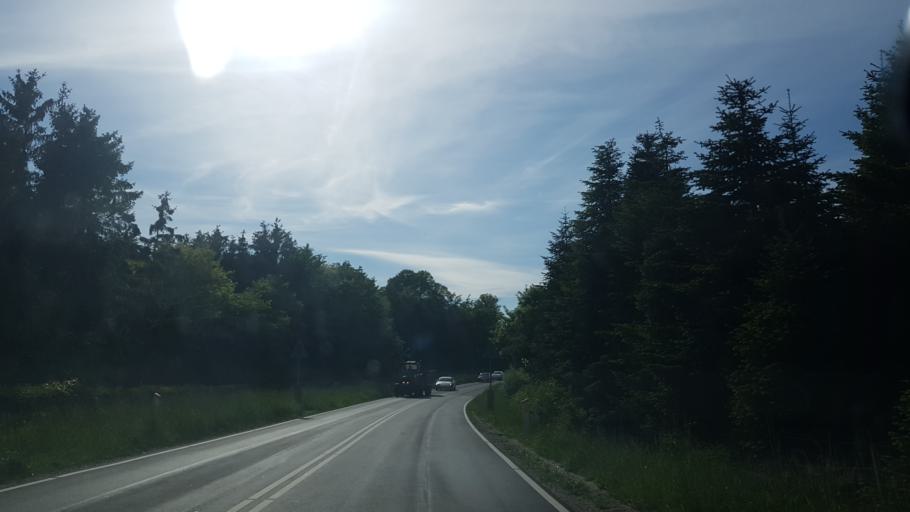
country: DK
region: Zealand
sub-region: Slagelse Kommune
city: Slagelse
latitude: 55.4167
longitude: 11.3194
